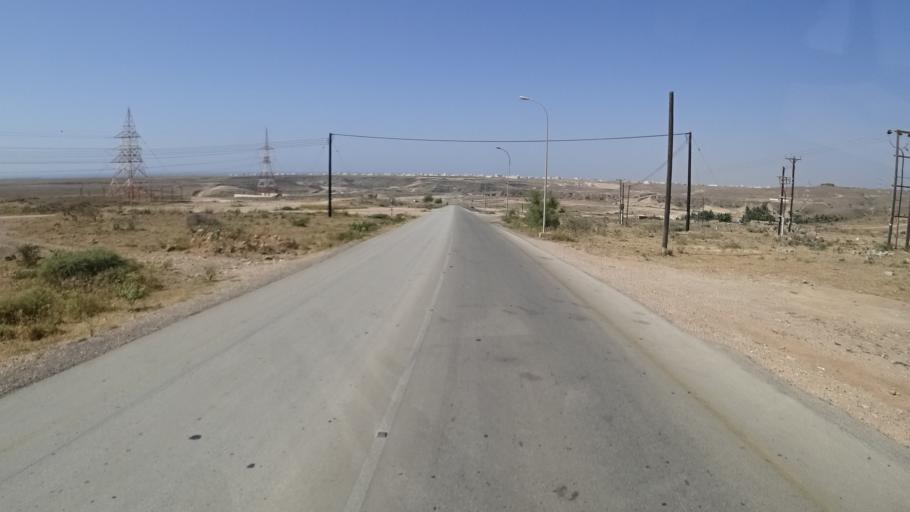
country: OM
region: Zufar
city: Salalah
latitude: 17.0657
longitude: 54.4379
